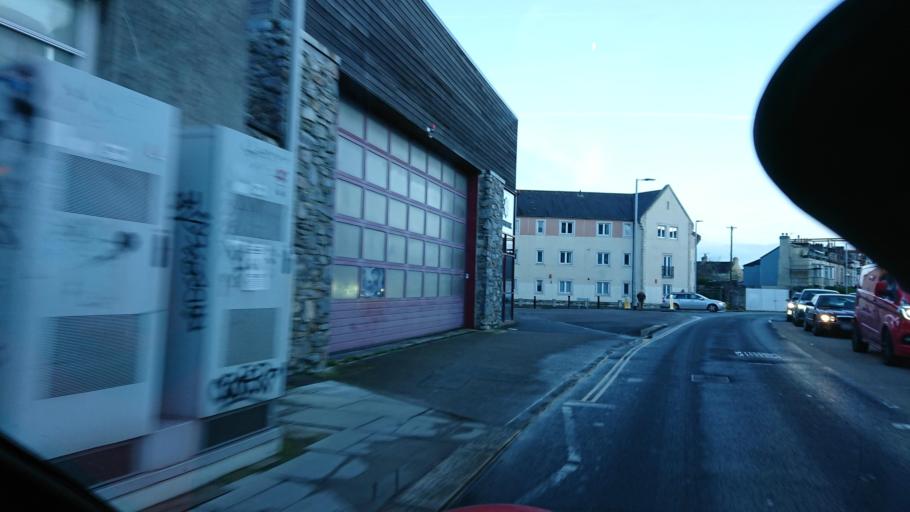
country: GB
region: England
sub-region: Plymouth
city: Plymouth
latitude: 50.3788
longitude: -4.1309
